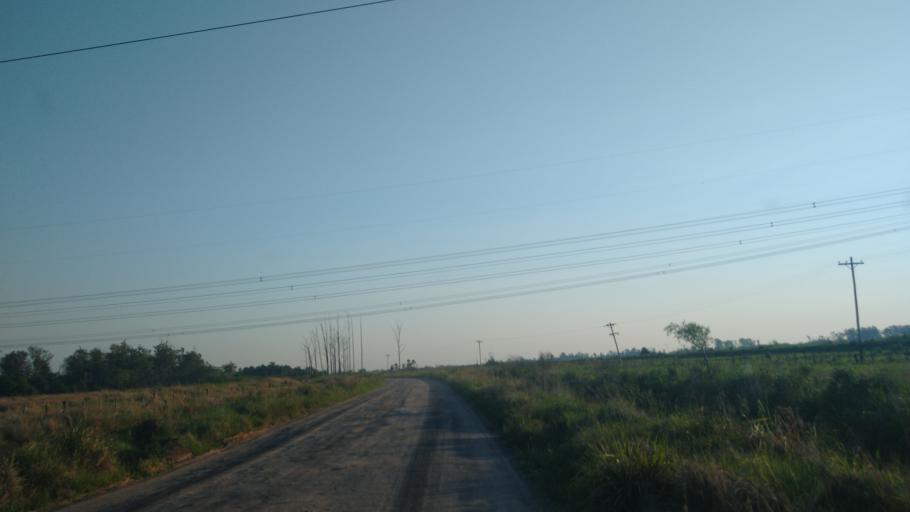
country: PY
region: Neembucu
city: Cerrito
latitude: -27.4017
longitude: -57.6595
